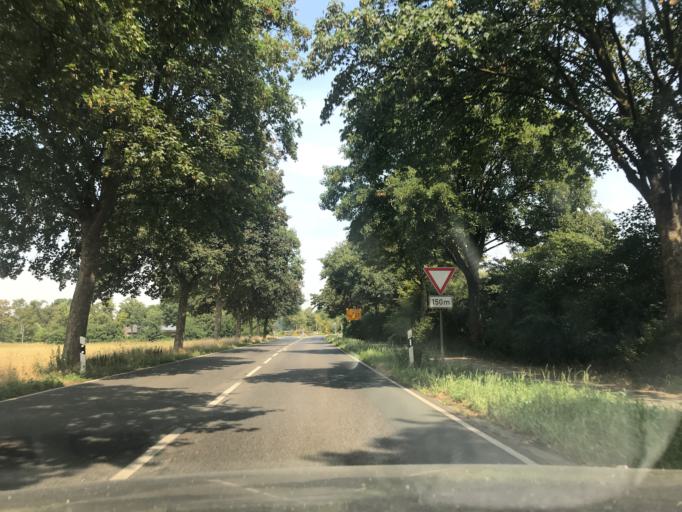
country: DE
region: North Rhine-Westphalia
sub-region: Regierungsbezirk Dusseldorf
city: Issum
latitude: 51.4928
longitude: 6.4170
